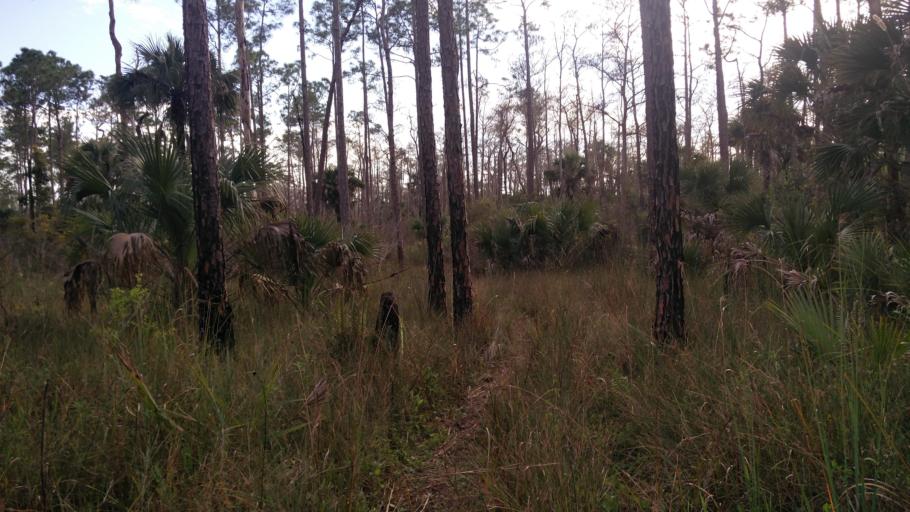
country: US
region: Florida
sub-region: Collier County
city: Lely Resort
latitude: 26.0018
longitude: -81.5828
